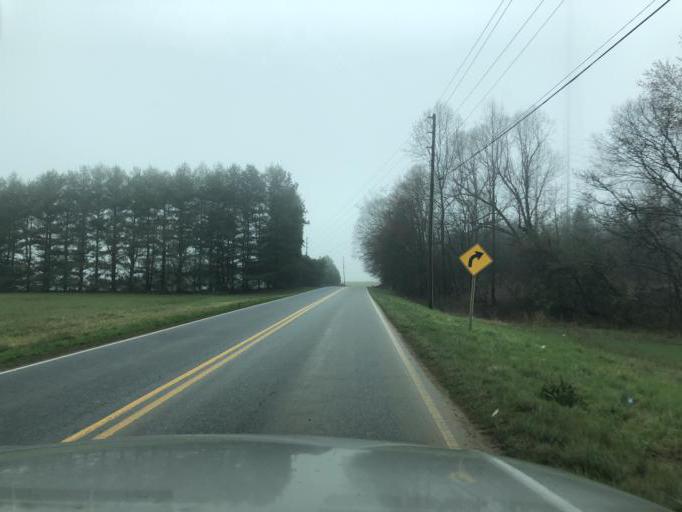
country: US
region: North Carolina
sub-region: Cleveland County
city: Shelby
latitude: 35.3385
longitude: -81.4606
